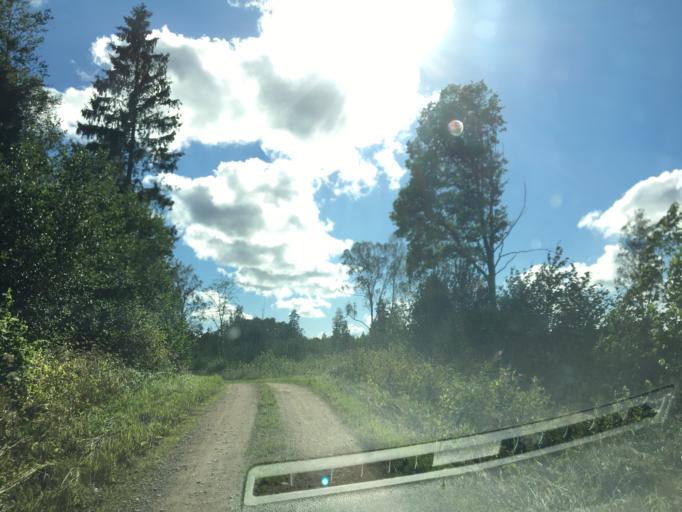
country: EE
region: Viljandimaa
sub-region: Suure-Jaani vald
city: Suure-Jaani
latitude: 58.5050
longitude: 25.2694
